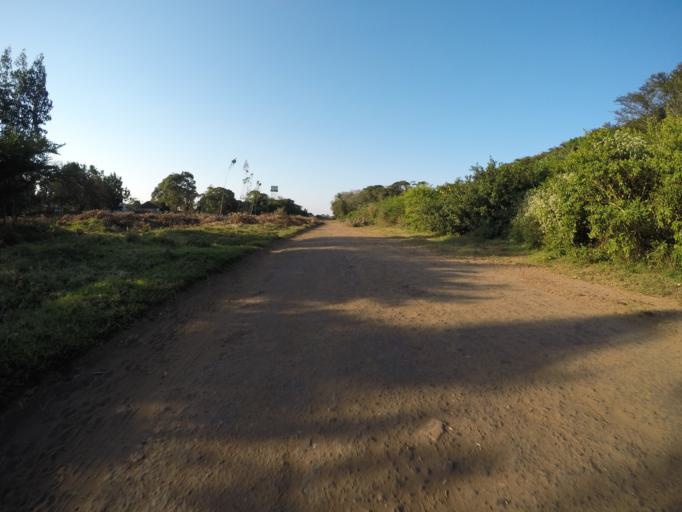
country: ZA
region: KwaZulu-Natal
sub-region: uThungulu District Municipality
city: KwaMbonambi
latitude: -28.6954
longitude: 32.1970
